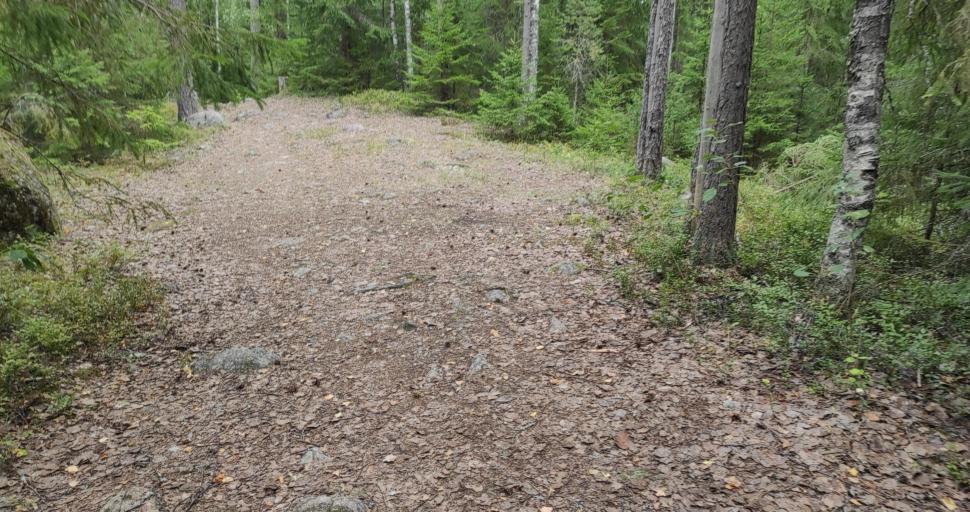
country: RU
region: Leningrad
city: Veshchevo
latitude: 60.6728
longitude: 29.2314
